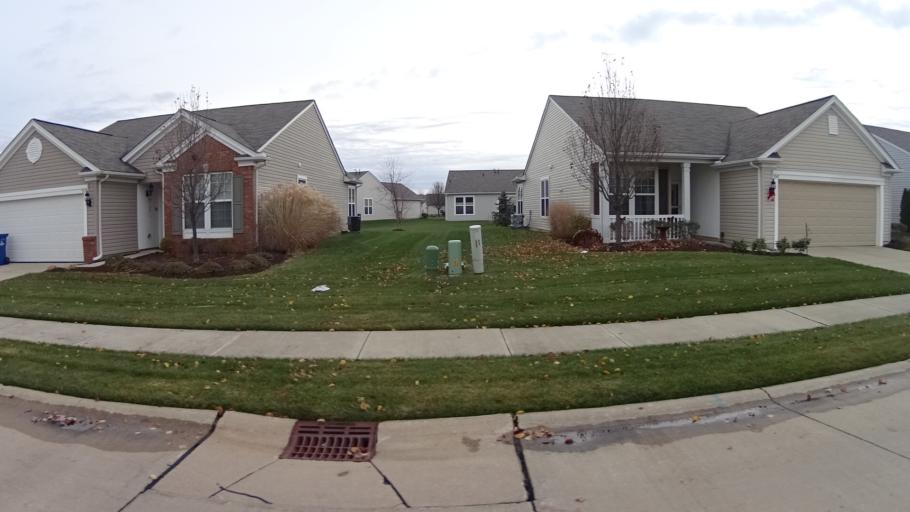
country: US
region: Ohio
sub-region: Lorain County
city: North Ridgeville
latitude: 41.3557
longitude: -82.0559
